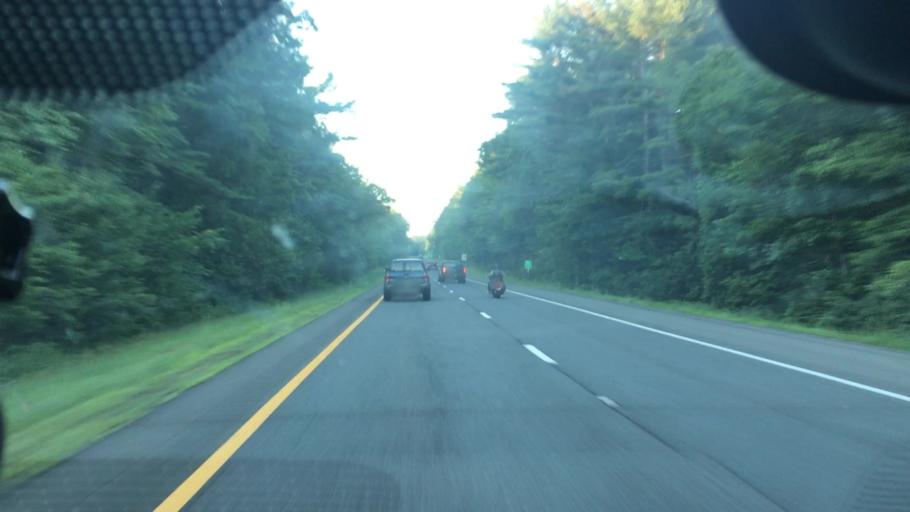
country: US
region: Massachusetts
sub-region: Franklin County
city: Turners Falls
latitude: 42.6235
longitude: -72.5863
